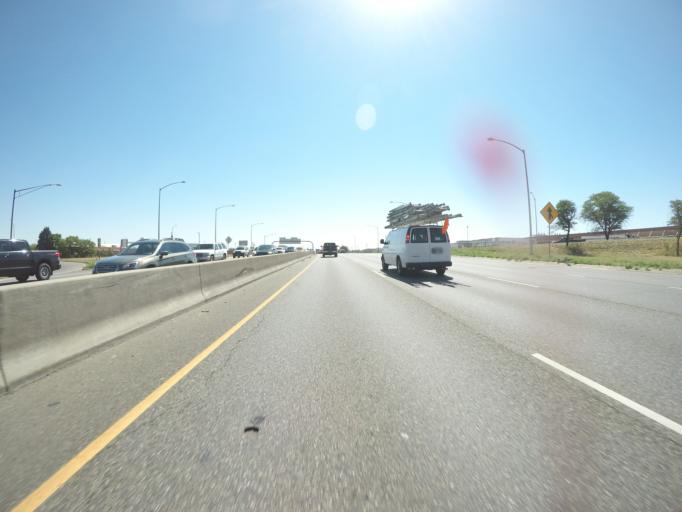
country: US
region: Colorado
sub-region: Adams County
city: Commerce City
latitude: 39.7800
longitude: -104.9400
